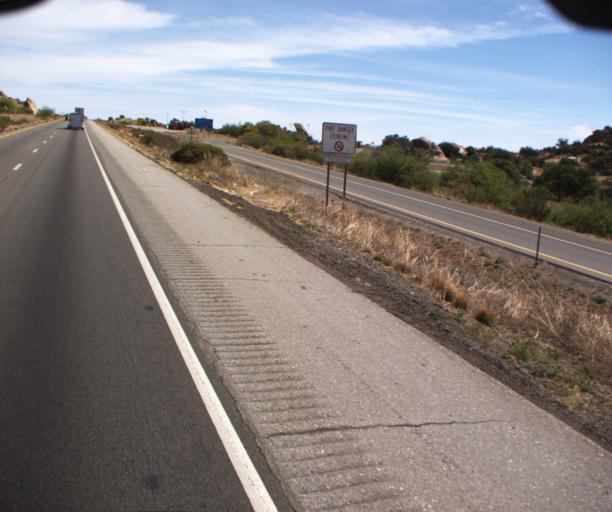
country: US
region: Arizona
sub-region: Cochise County
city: Saint David
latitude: 32.0580
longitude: -110.0792
